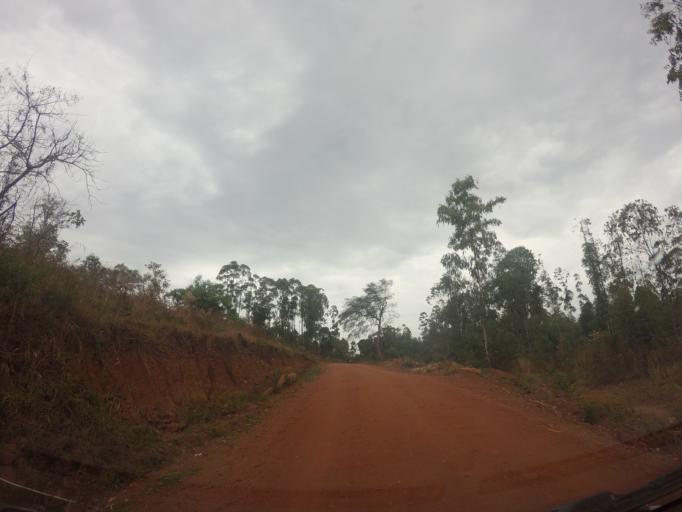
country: UG
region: Northern Region
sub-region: Zombo District
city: Zombo
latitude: 2.7668
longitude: 30.8581
